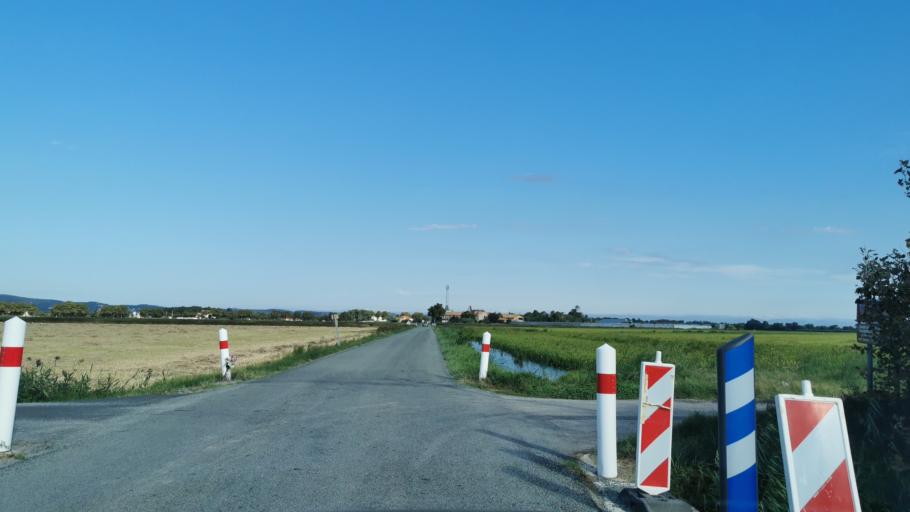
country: FR
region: Languedoc-Roussillon
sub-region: Departement de l'Aude
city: Gruissan
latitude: 43.1150
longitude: 3.0405
